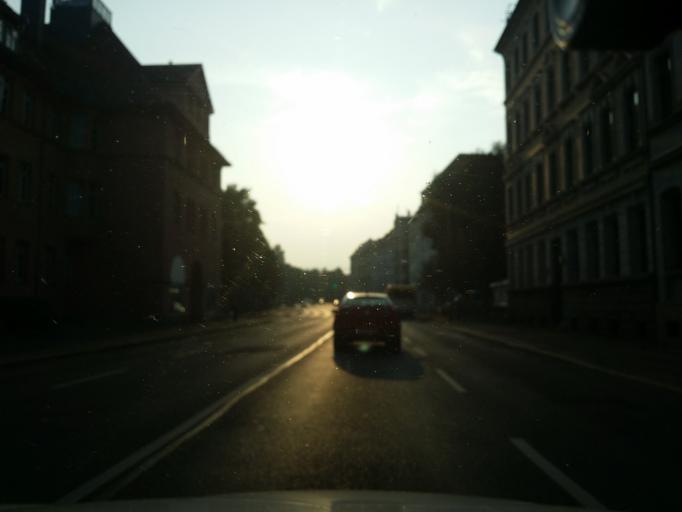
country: DE
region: Saxony
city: Leipzig
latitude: 51.3188
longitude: 12.3438
